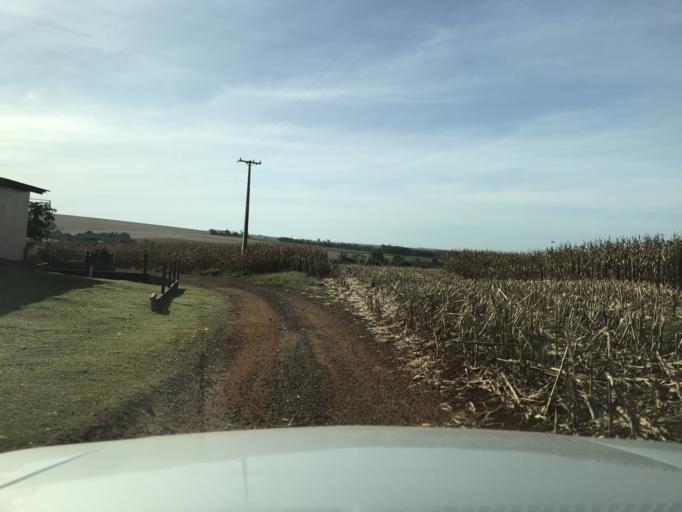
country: BR
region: Parana
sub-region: Palotina
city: Palotina
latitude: -24.2586
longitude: -53.7486
